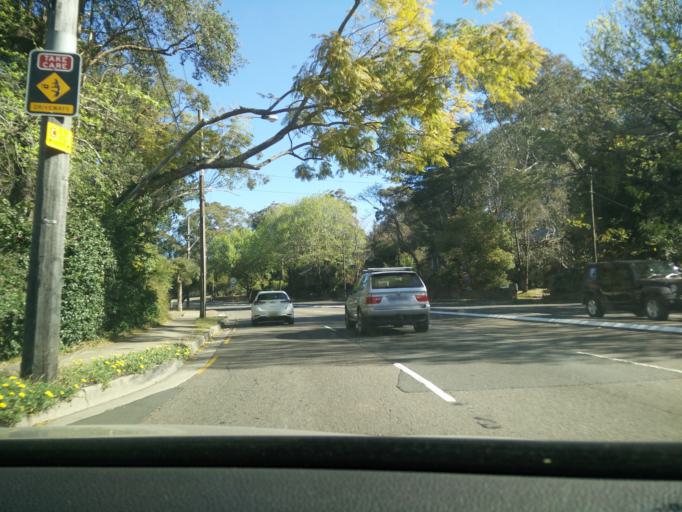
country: AU
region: New South Wales
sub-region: City of Sydney
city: Pymble
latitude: -33.7562
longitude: 151.1380
